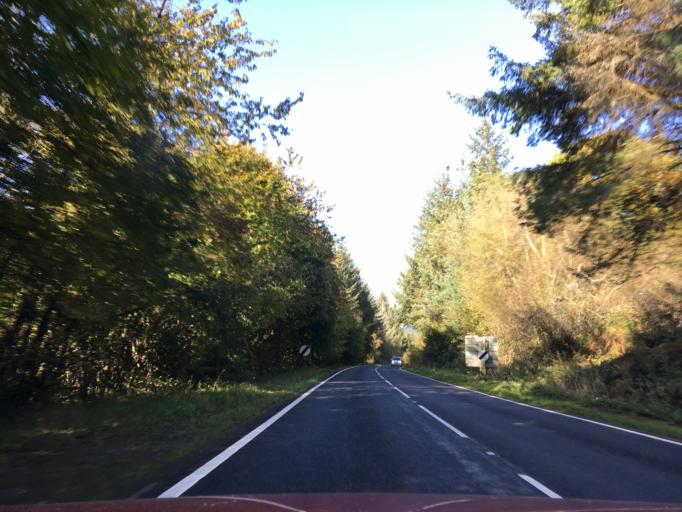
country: GB
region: Wales
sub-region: Merthyr Tydfil County Borough
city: Merthyr Tydfil
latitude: 51.7980
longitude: -3.4378
